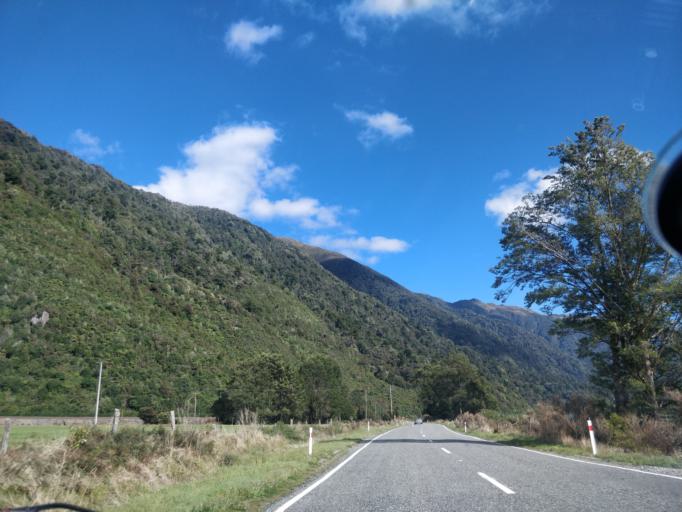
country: NZ
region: West Coast
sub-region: Grey District
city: Greymouth
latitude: -42.7620
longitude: 171.6081
